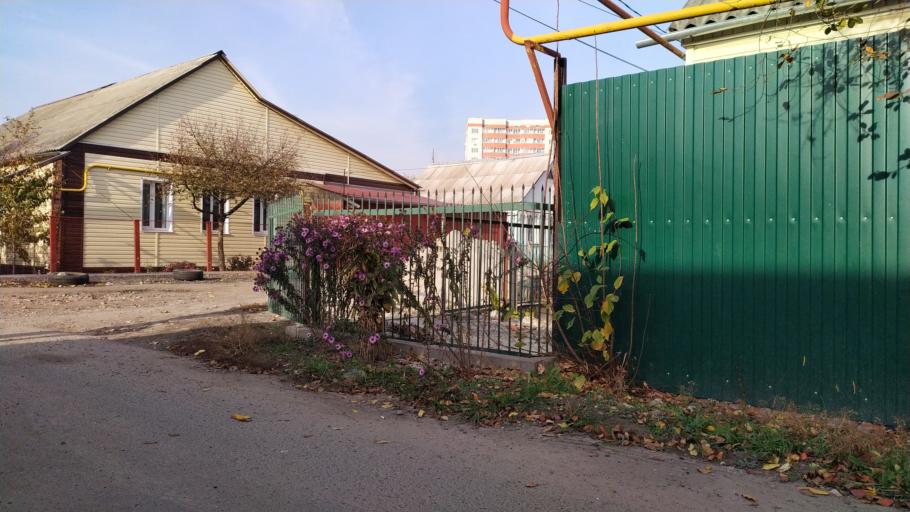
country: RU
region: Kursk
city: Kursk
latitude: 51.6463
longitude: 36.1442
